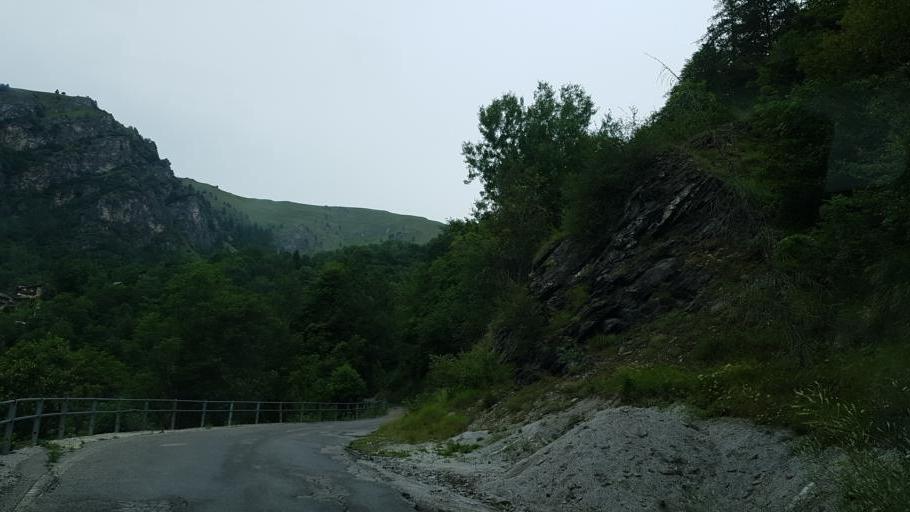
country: IT
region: Piedmont
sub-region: Provincia di Cuneo
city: Stroppo
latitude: 44.5186
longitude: 7.1288
